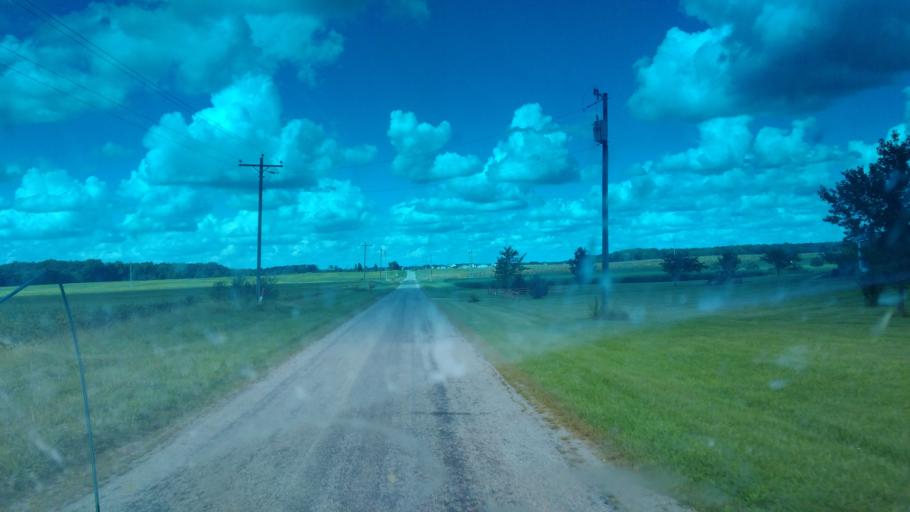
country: US
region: Ohio
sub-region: Union County
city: Richwood
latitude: 40.4579
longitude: -83.4946
